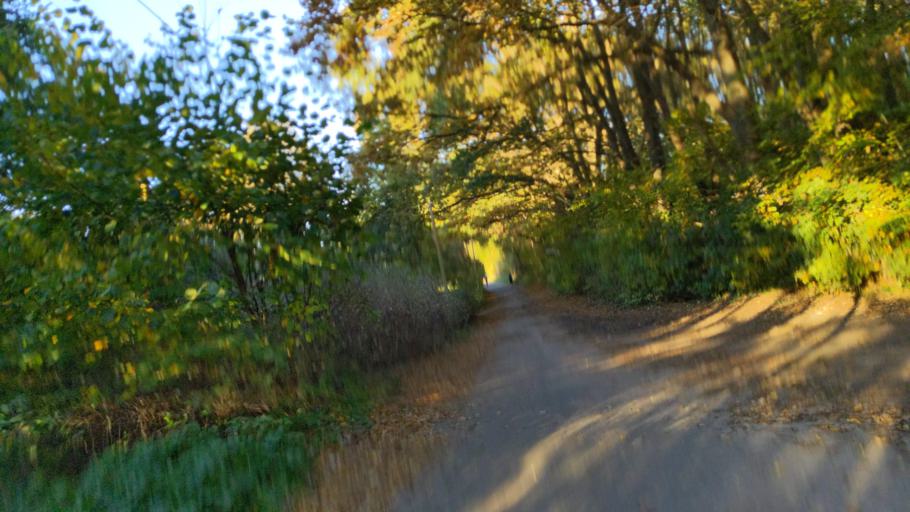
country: DE
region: Schleswig-Holstein
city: Gross Gronau
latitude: 53.8416
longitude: 10.7376
